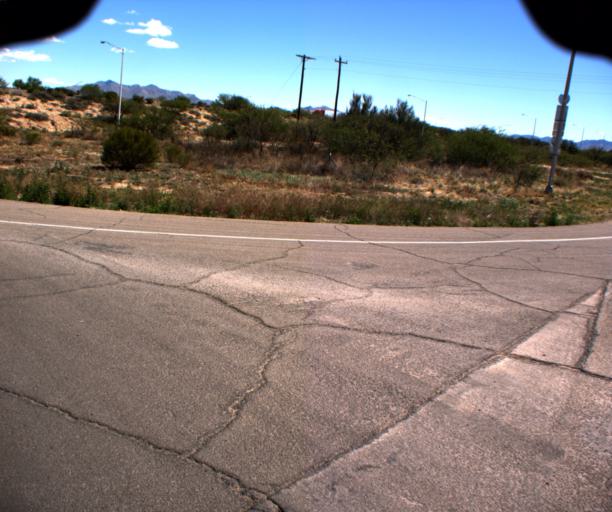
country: US
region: Arizona
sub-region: Cochise County
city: Benson
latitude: 31.9650
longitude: -110.2739
